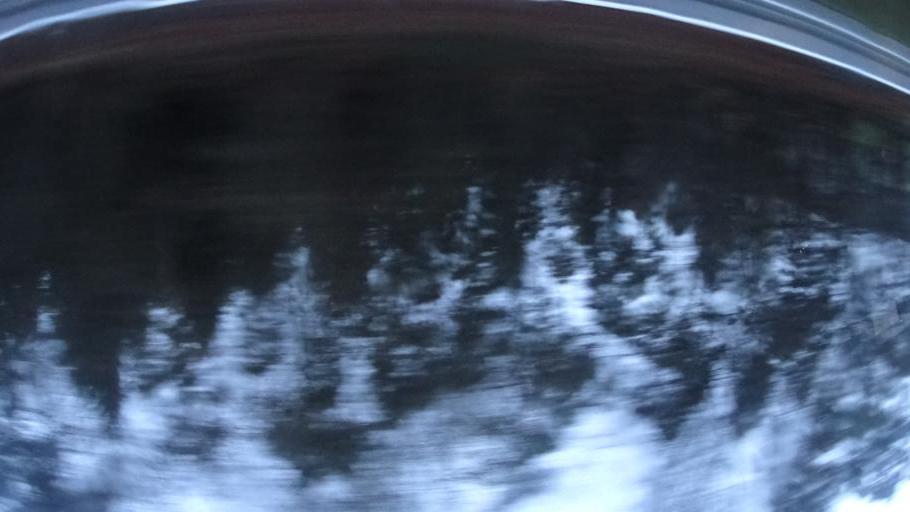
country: DE
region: Hesse
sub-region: Regierungsbezirk Kassel
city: Eichenzell
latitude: 50.4768
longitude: 9.6942
